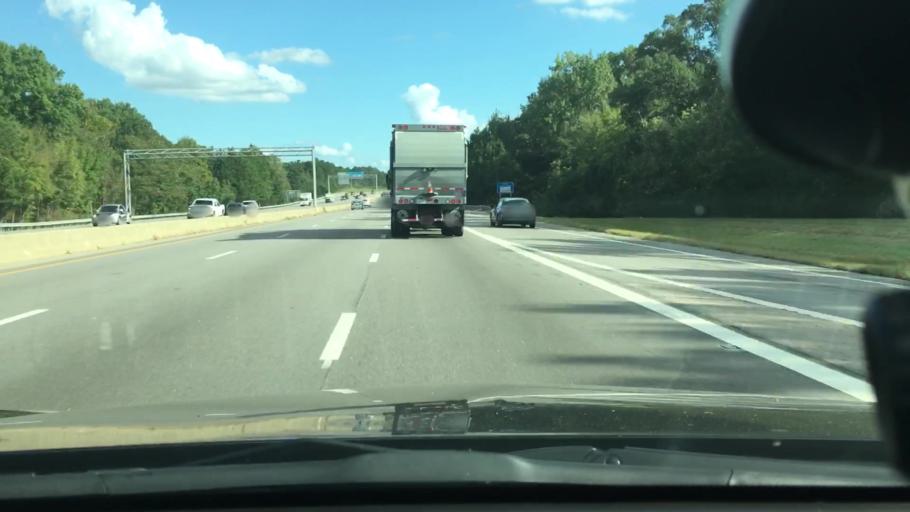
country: US
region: North Carolina
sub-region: Wake County
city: Raleigh
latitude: 35.7927
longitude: -78.5803
